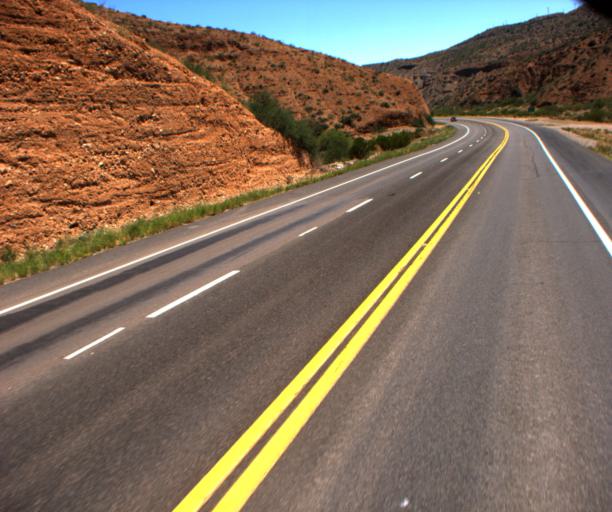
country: US
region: Arizona
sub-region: Greenlee County
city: Clifton
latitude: 33.0629
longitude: -109.3240
